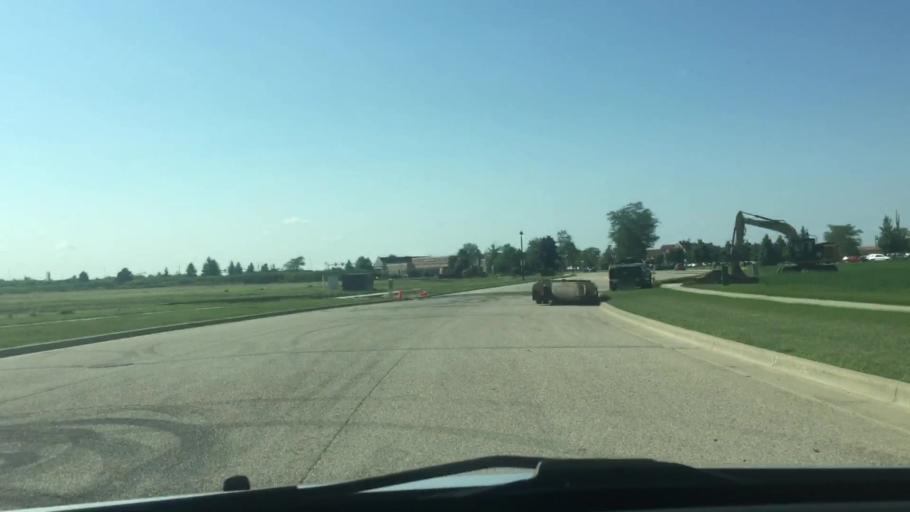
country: US
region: Wisconsin
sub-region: Waukesha County
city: Oconomowoc
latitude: 43.0724
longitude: -88.4657
